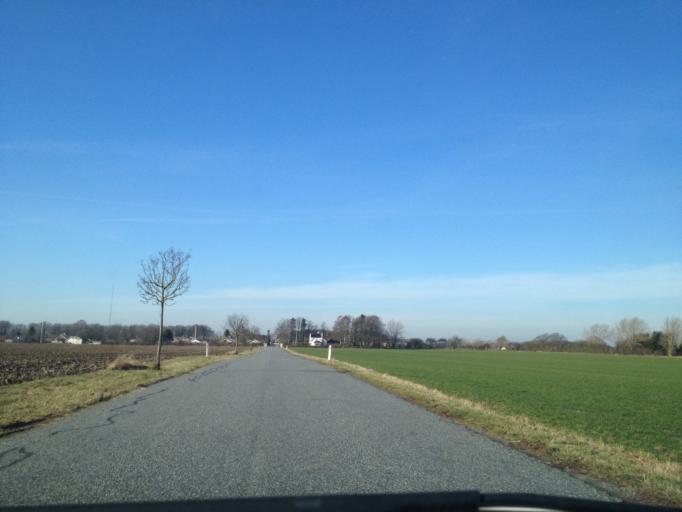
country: DK
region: South Denmark
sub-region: Nyborg Kommune
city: Ullerslev
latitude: 55.3914
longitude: 10.6981
